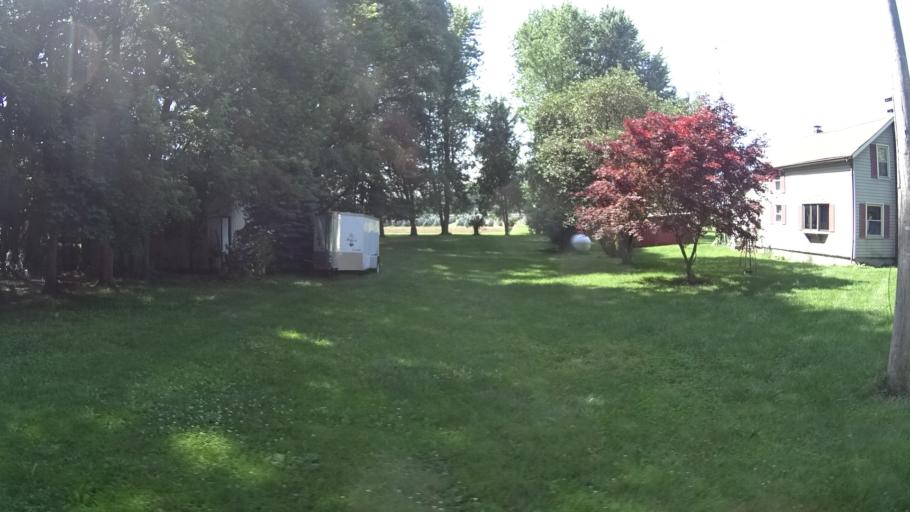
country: US
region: Ohio
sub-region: Erie County
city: Huron
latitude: 41.3721
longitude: -82.4906
